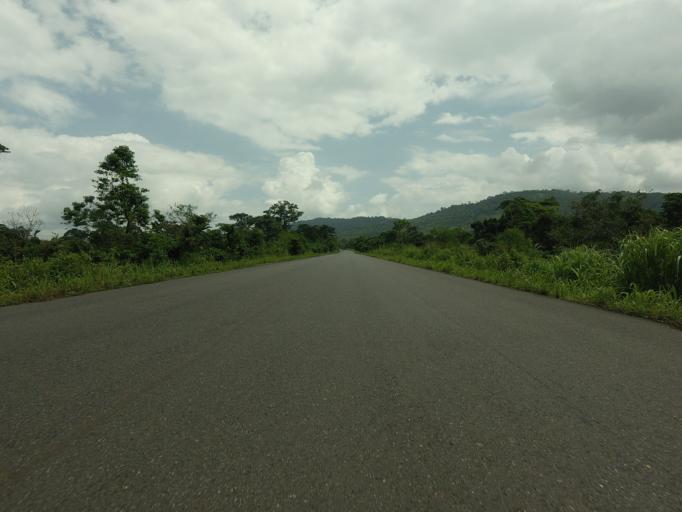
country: GH
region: Volta
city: Ho
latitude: 6.5404
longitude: 0.2400
